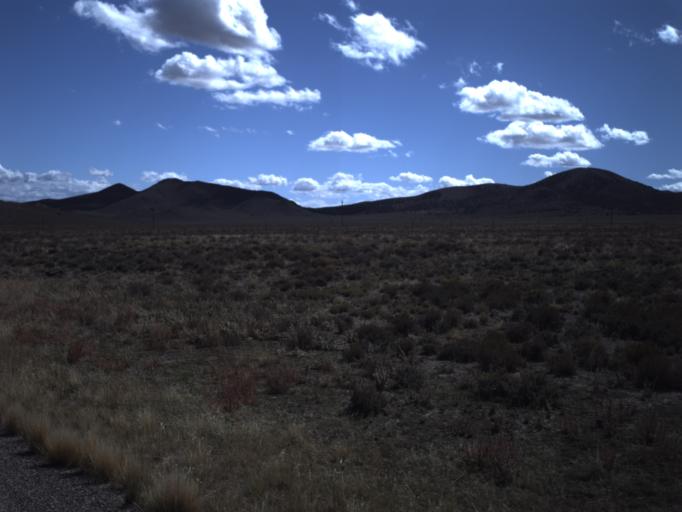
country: US
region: Utah
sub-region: Beaver County
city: Milford
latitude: 38.4289
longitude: -113.1236
